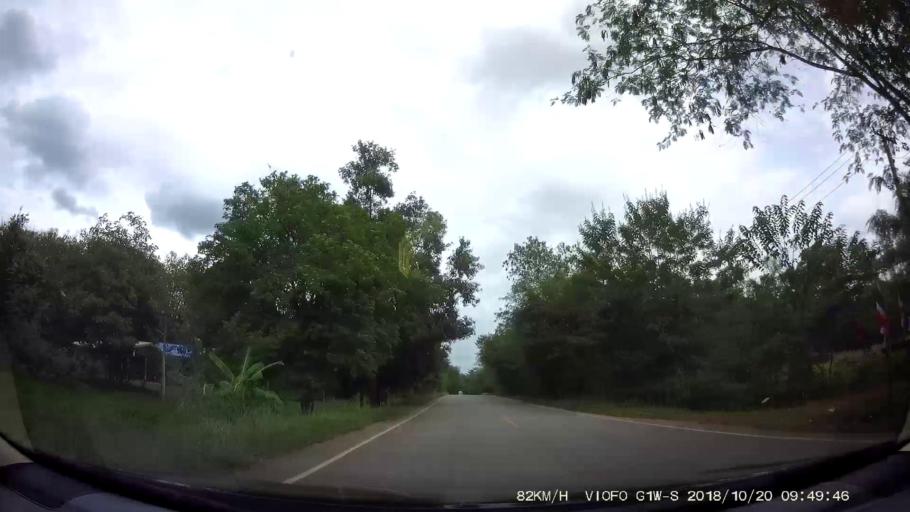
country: TH
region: Chaiyaphum
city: Khon San
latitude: 16.5234
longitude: 101.9041
